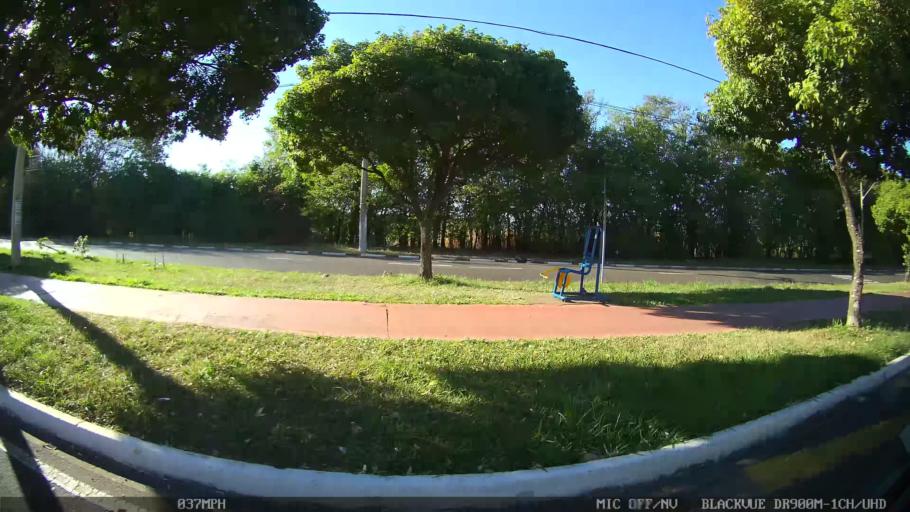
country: BR
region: Sao Paulo
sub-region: Franca
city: Franca
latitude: -20.5697
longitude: -47.3668
